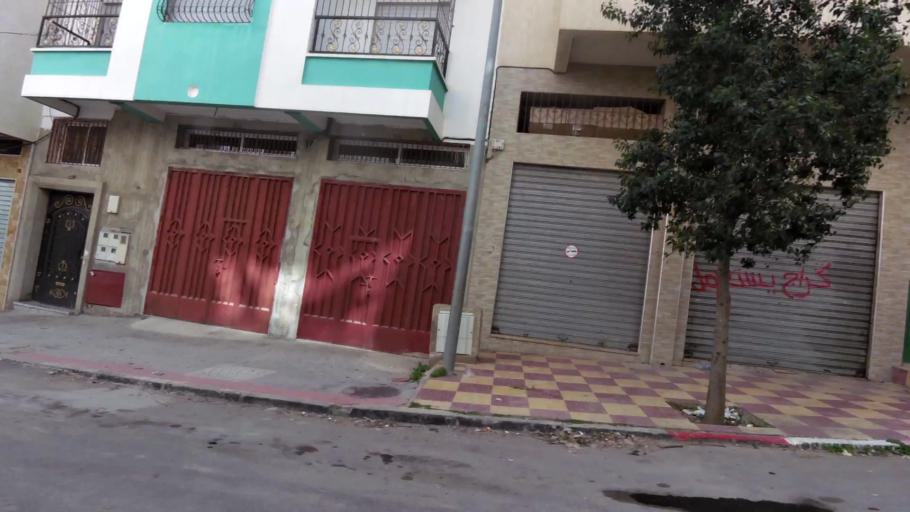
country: MA
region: Tanger-Tetouan
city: Tetouan
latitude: 35.5857
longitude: -5.3575
